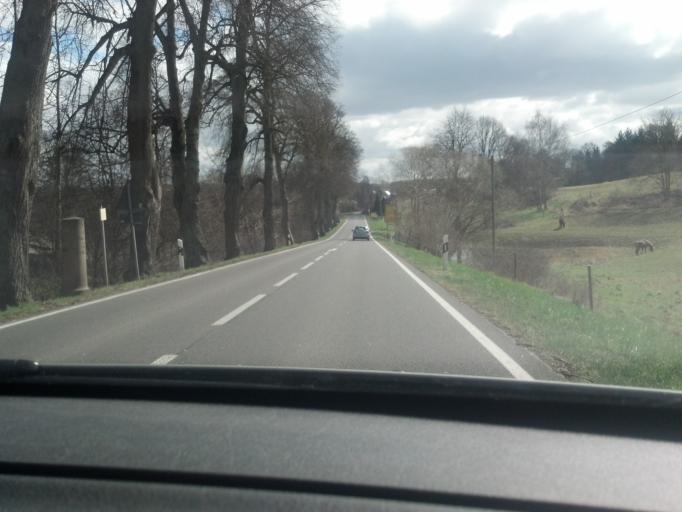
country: DE
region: Mecklenburg-Vorpommern
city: Loitz
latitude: 53.3410
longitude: 13.4241
